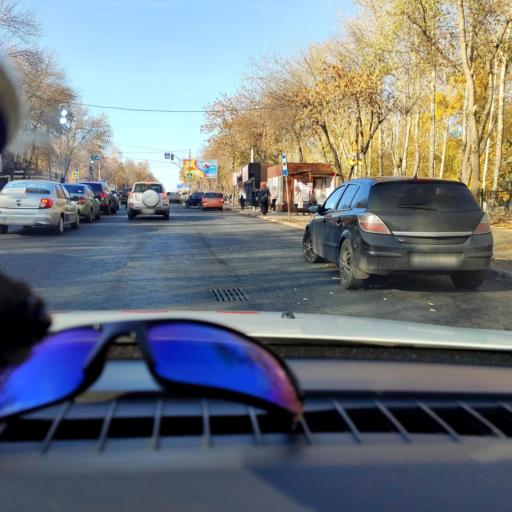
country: RU
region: Samara
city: Samara
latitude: 53.2155
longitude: 50.2105
